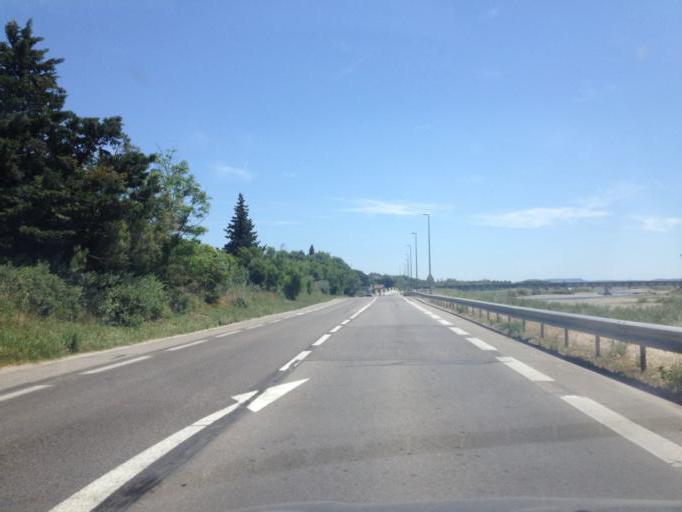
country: FR
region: Provence-Alpes-Cote d'Azur
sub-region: Departement du Vaucluse
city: Cavaillon
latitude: 43.8321
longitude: 5.0258
